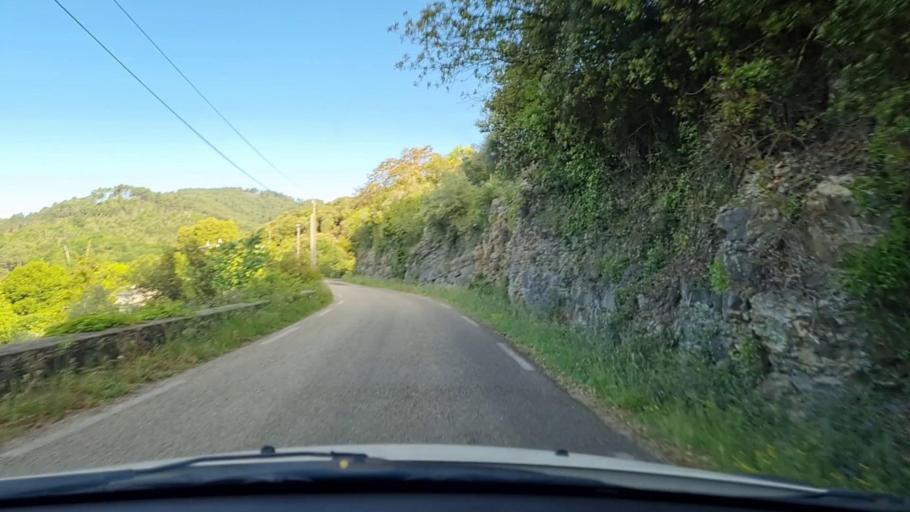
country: FR
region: Languedoc-Roussillon
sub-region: Departement du Gard
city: Cendras
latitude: 44.1594
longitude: 4.0332
